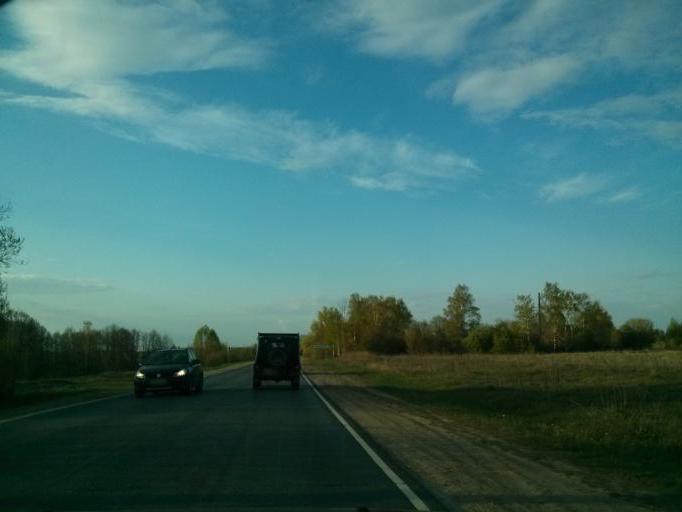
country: RU
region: Nizjnij Novgorod
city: Navashino
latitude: 55.6225
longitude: 42.2303
